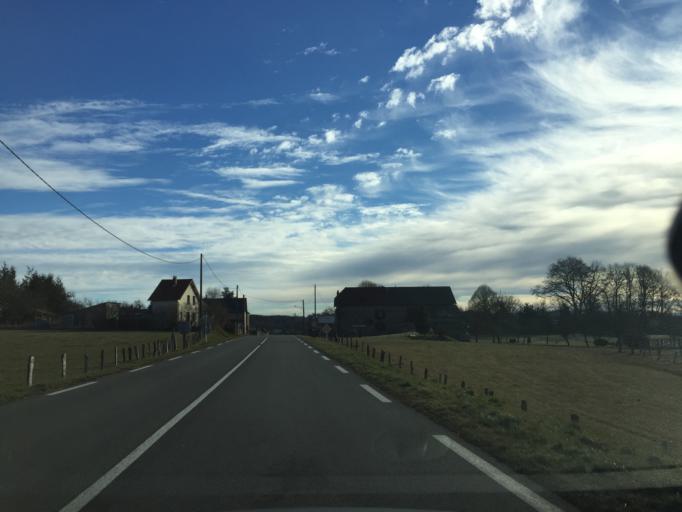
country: FR
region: Limousin
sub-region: Departement de la Creuse
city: Auzances
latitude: 45.8882
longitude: 2.4862
